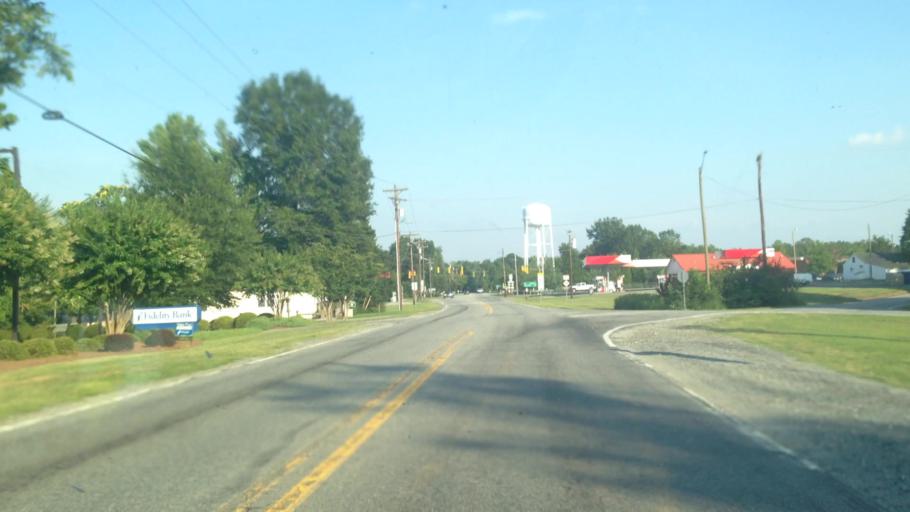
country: US
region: North Carolina
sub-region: Guilford County
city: Stokesdale
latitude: 36.2386
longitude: -79.9810
